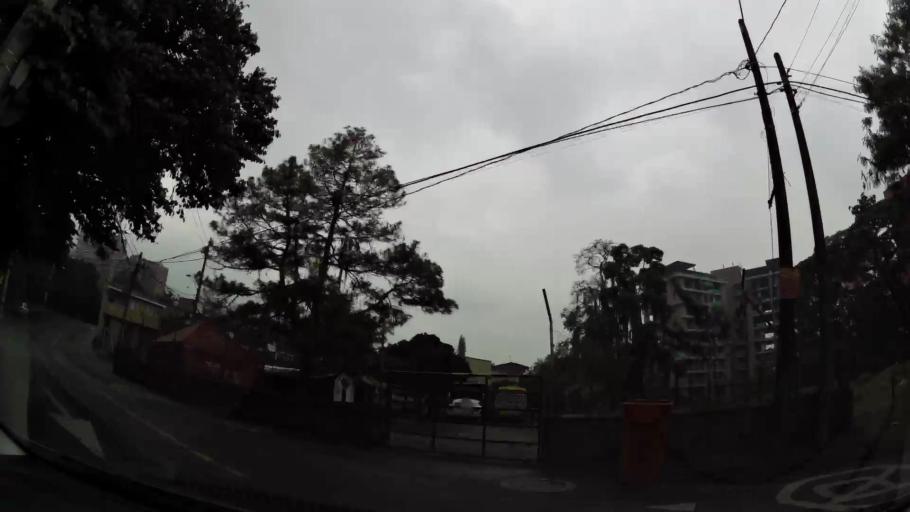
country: CO
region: Antioquia
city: Envigado
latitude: 6.1792
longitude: -75.5620
